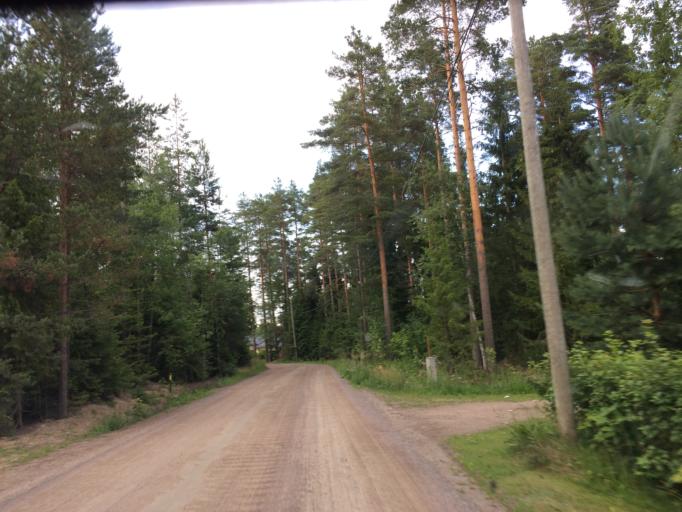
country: FI
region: Haeme
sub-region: Haemeenlinna
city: Tervakoski
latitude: 60.8509
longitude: 24.6226
